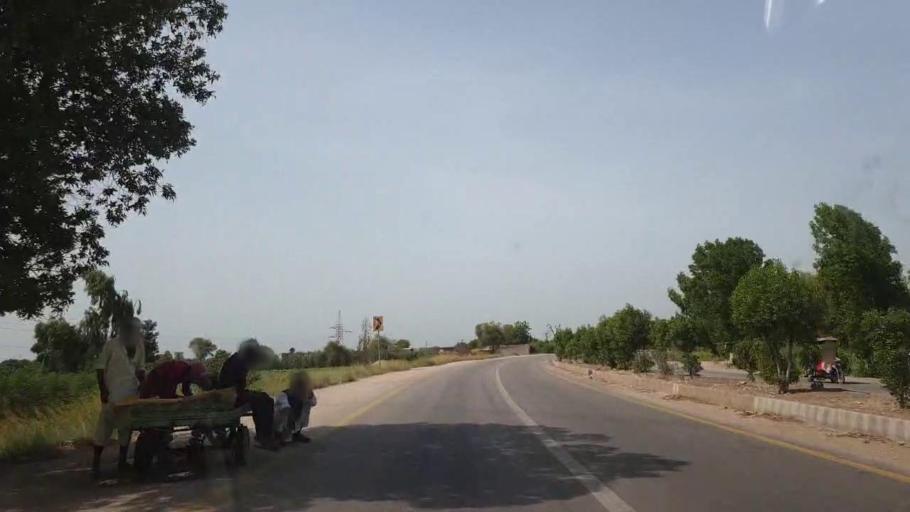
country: PK
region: Sindh
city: Sakrand
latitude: 26.1916
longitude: 68.2912
